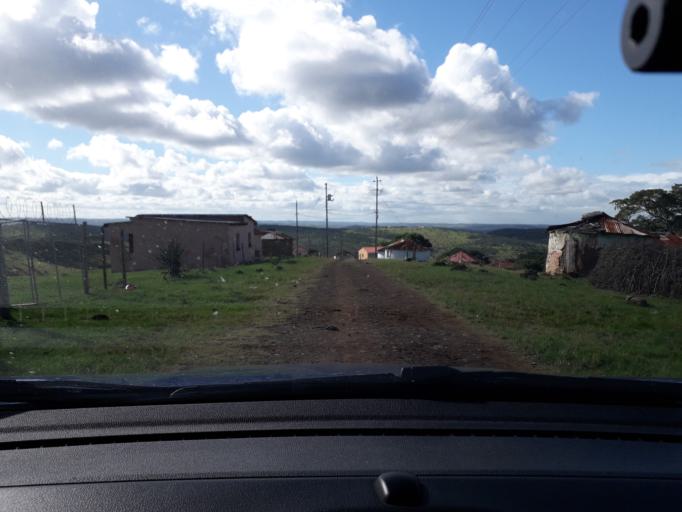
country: ZA
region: Eastern Cape
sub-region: Buffalo City Metropolitan Municipality
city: Bhisho
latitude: -33.1104
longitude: 27.4274
